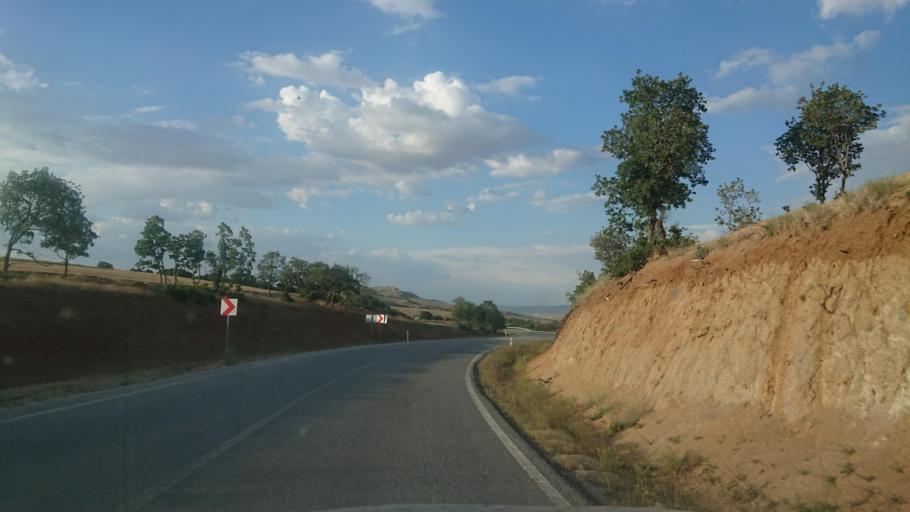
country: TR
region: Aksaray
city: Balci
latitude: 38.6216
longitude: 34.0960
